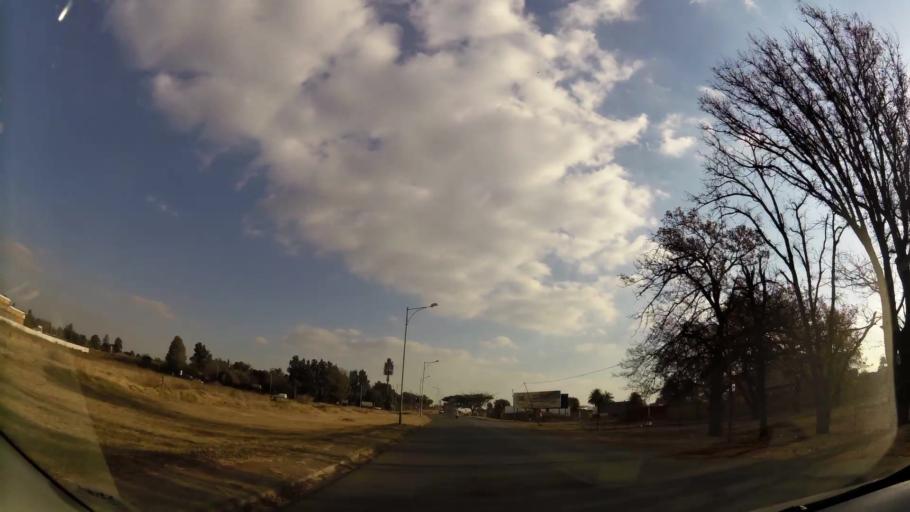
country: ZA
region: Gauteng
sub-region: West Rand District Municipality
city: Krugersdorp
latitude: -26.1005
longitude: 27.7400
